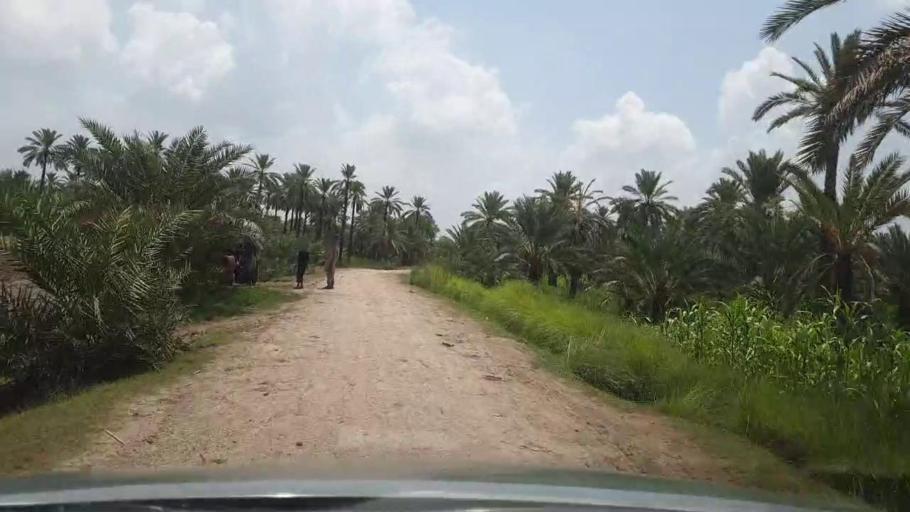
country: PK
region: Sindh
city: Khairpur
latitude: 27.6289
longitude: 68.7391
